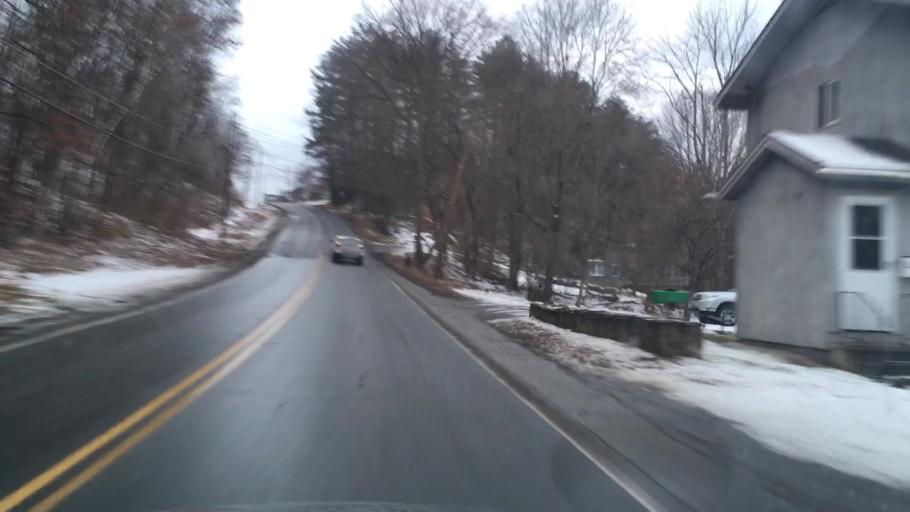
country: US
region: New Hampshire
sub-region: Sullivan County
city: Claremont
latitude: 43.3829
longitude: -72.3487
